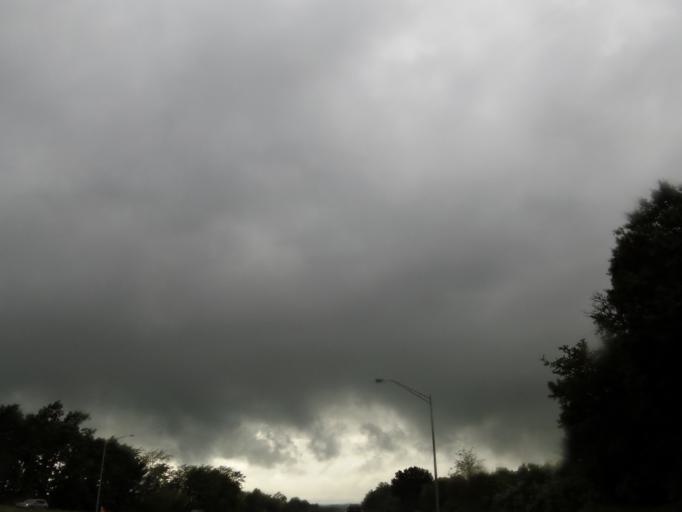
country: US
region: Illinois
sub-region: Jefferson County
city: Mount Vernon
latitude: 38.3391
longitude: -88.9612
